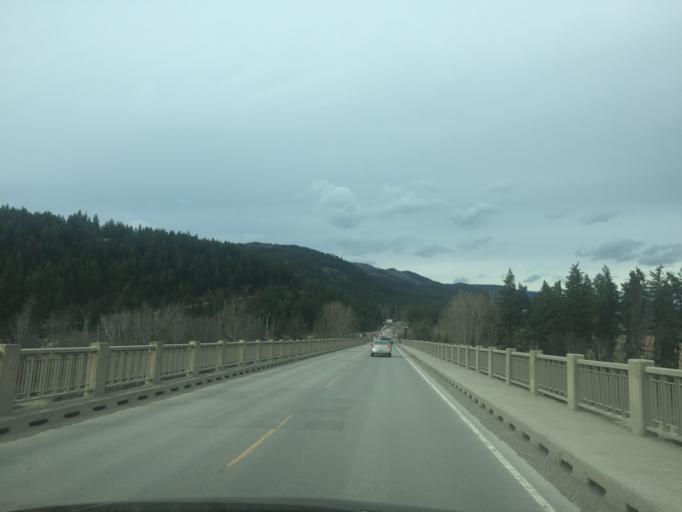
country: CA
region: British Columbia
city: Kamloops
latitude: 51.1886
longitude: -120.1480
